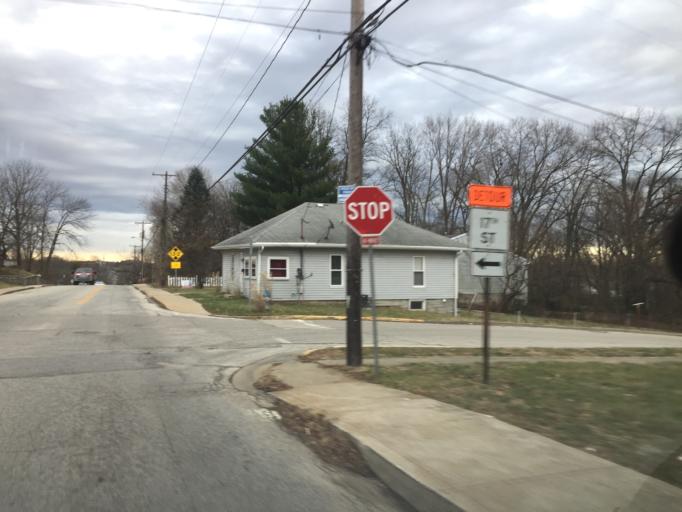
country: US
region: Indiana
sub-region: Monroe County
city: Bloomington
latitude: 39.1732
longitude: -86.5474
